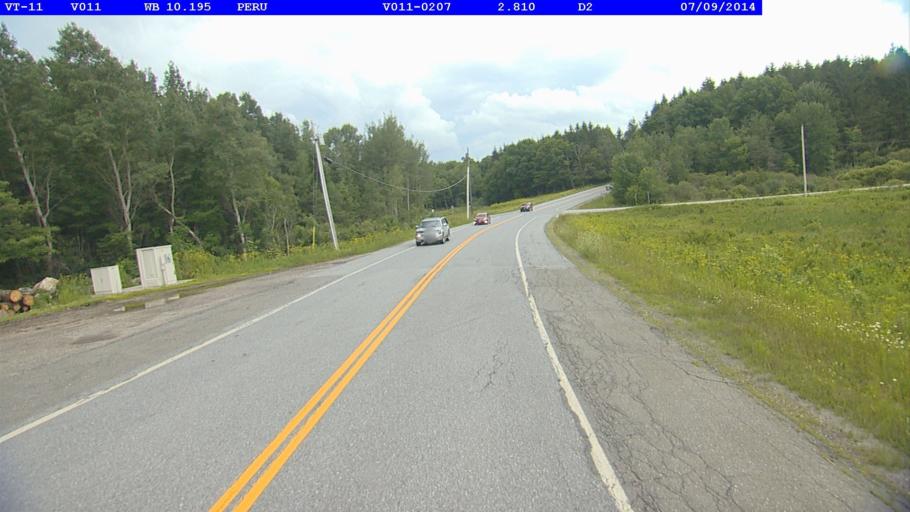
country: US
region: Vermont
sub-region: Bennington County
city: Manchester Center
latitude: 43.2295
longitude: -72.8975
